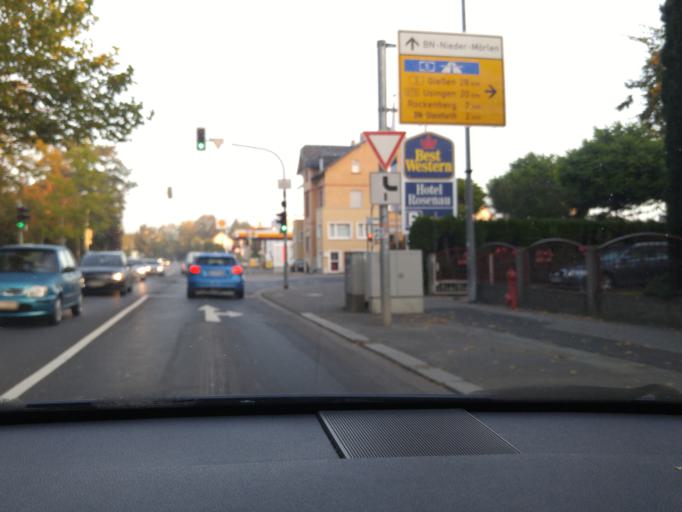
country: DE
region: Hesse
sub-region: Regierungsbezirk Darmstadt
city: Bad Nauheim
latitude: 50.3751
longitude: 8.7406
